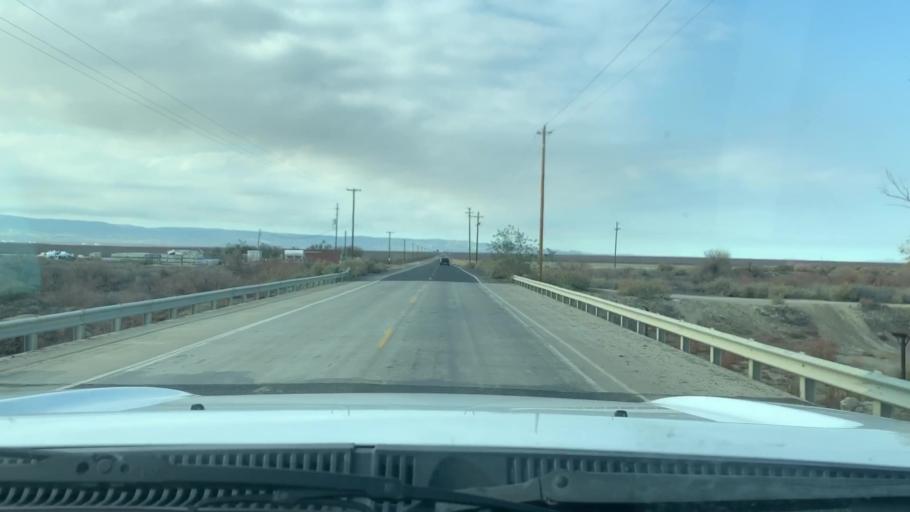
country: US
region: California
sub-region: Kern County
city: Lost Hills
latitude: 35.4995
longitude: -119.6182
